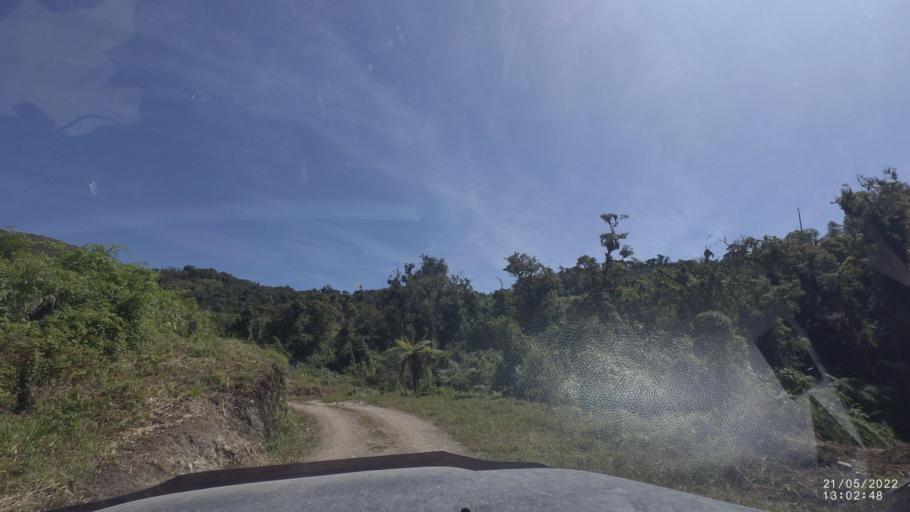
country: BO
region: Cochabamba
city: Colomi
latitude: -17.1600
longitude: -65.9517
